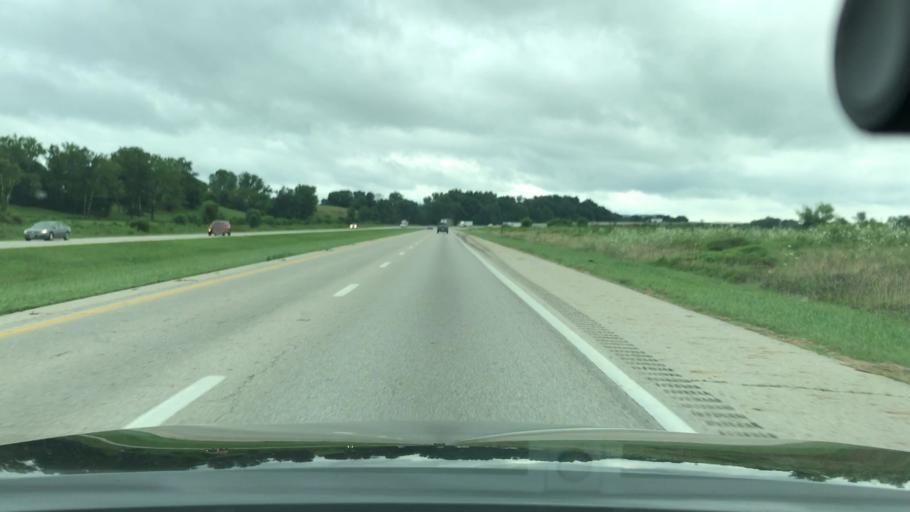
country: US
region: Ohio
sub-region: Ross County
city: Chillicothe
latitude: 39.2845
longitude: -82.8891
